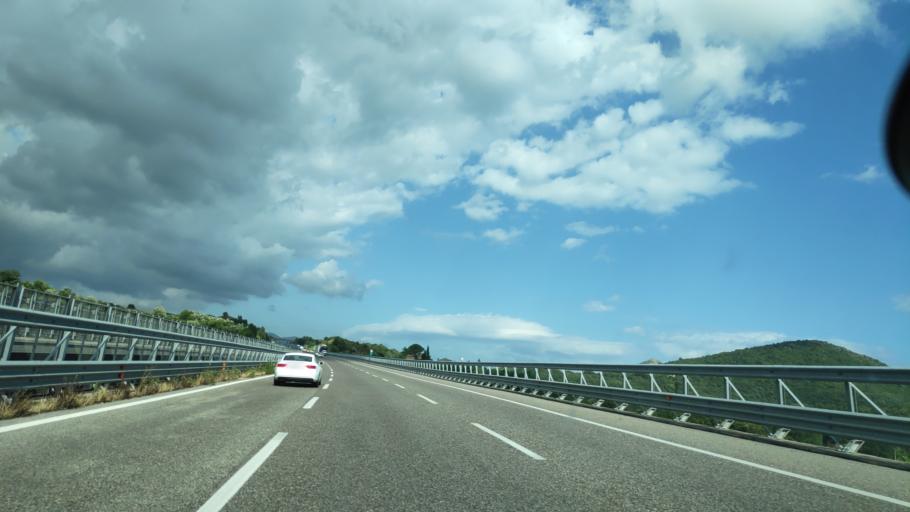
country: IT
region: Campania
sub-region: Provincia di Salerno
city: Contursi Terme
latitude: 40.6119
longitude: 15.2553
